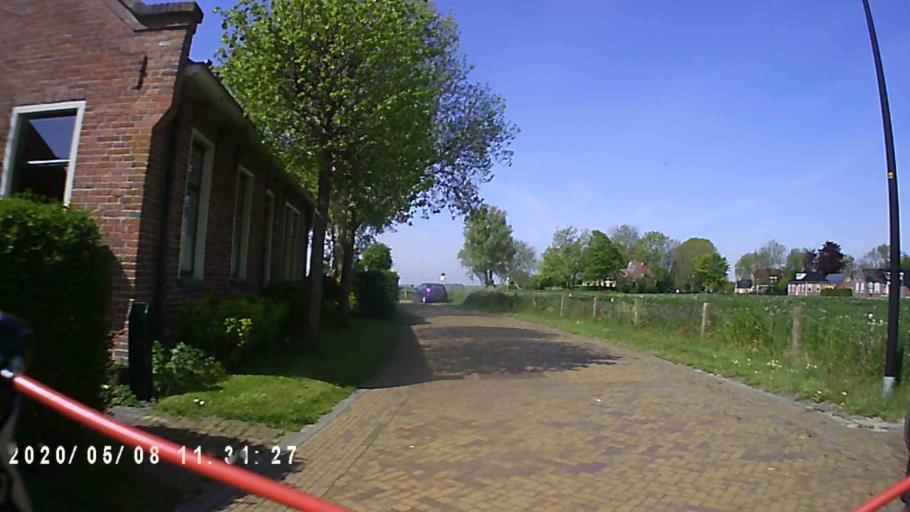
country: NL
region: Groningen
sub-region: Gemeente Bedum
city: Bedum
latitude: 53.3452
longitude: 6.7083
